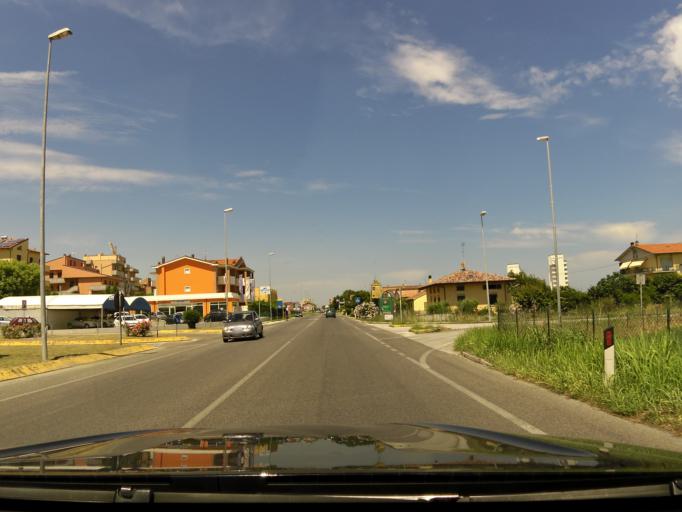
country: IT
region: The Marches
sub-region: Provincia di Pesaro e Urbino
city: Marotta
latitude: 43.7550
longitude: 13.1601
